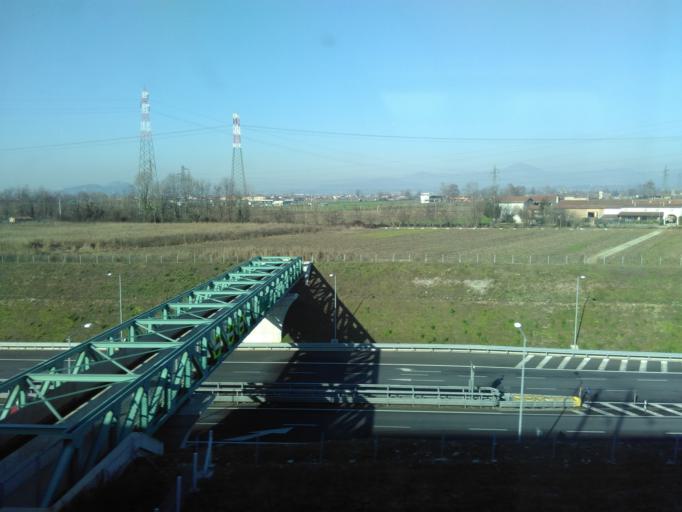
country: IT
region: Lombardy
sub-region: Provincia di Brescia
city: Travagliato
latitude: 45.5326
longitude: 10.0589
